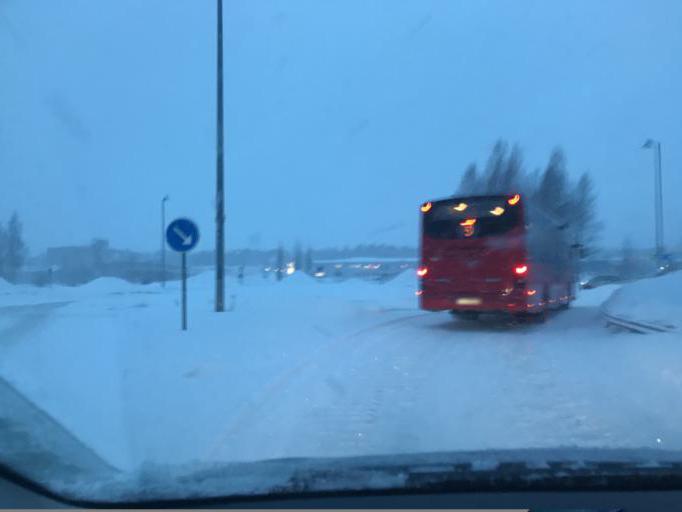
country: SE
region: Norrbotten
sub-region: Lulea Kommun
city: Bergnaset
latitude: 65.6126
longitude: 22.1225
